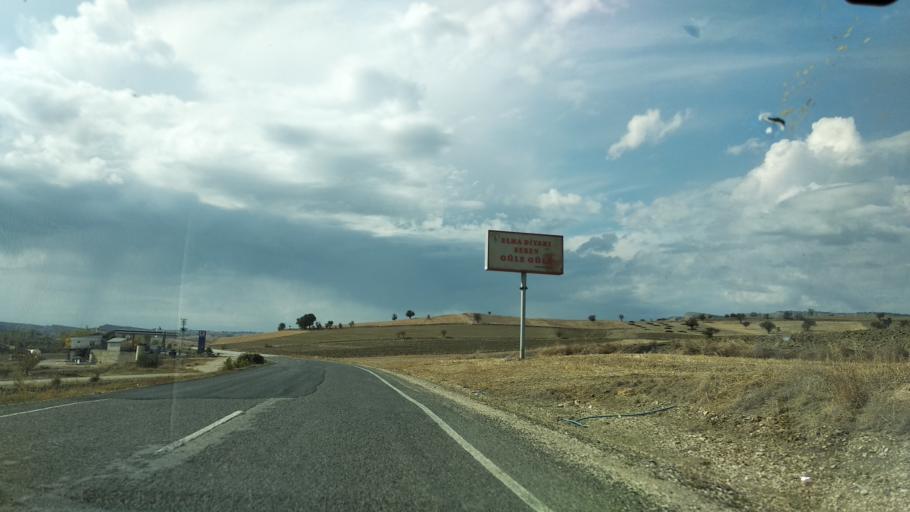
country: TR
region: Bolu
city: Seben
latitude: 40.4018
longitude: 31.5628
